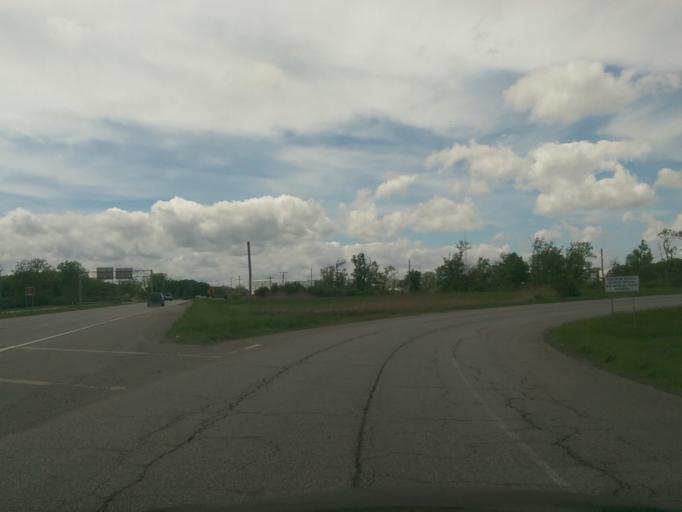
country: US
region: Indiana
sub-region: Lake County
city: East Chicago
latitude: 41.6041
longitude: -87.4337
